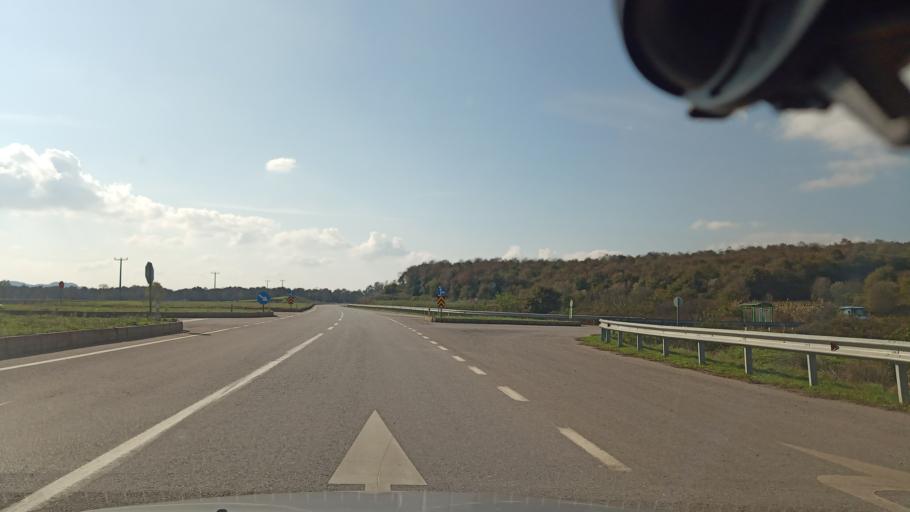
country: TR
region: Sakarya
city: Kaynarca
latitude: 41.0629
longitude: 30.3550
